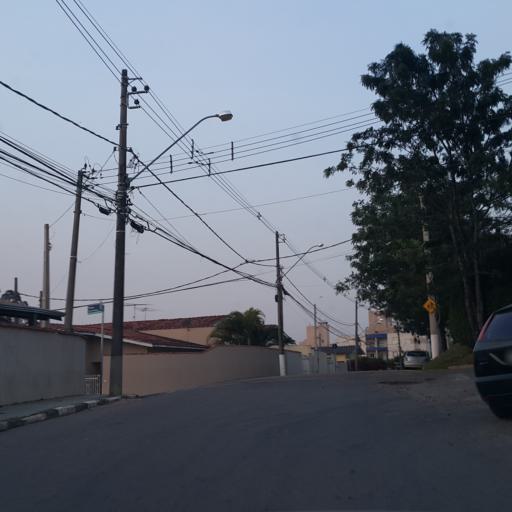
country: BR
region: Sao Paulo
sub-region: Vinhedo
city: Vinhedo
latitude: -23.0400
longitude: -46.9784
